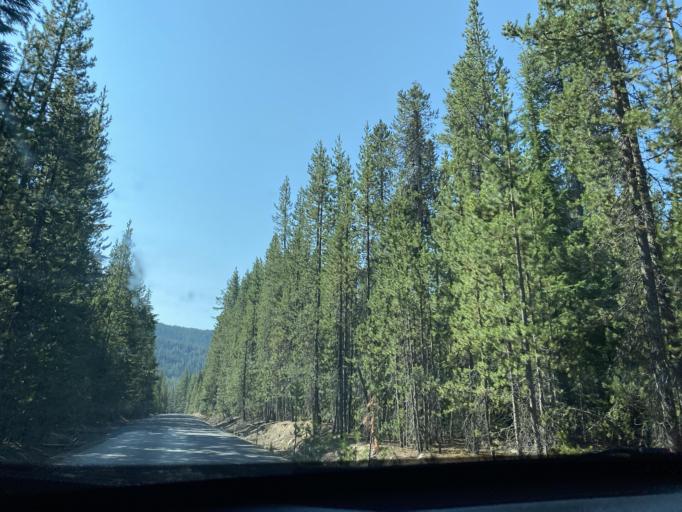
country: US
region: Oregon
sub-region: Deschutes County
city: Three Rivers
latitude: 43.7051
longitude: -121.2751
